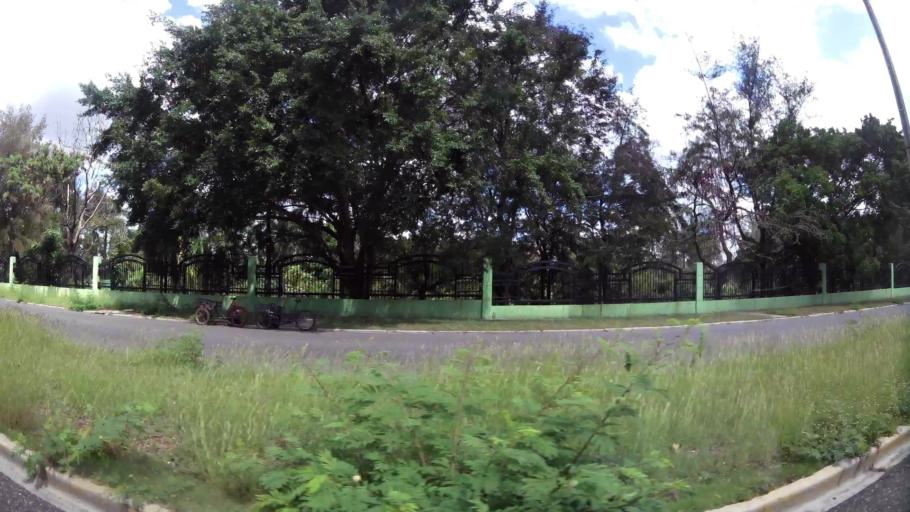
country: DO
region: Santo Domingo
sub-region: Santo Domingo
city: Santo Domingo Este
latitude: 18.4777
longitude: -69.8588
